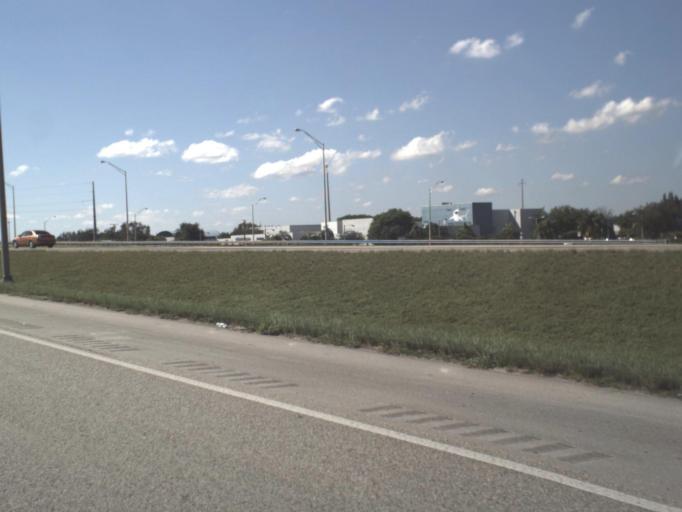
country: US
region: Florida
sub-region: Miami-Dade County
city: Sweetwater
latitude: 25.7711
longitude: -80.3859
